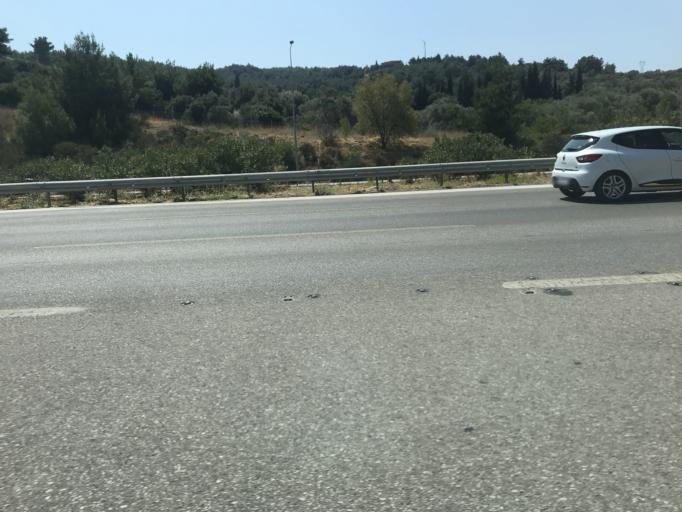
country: TR
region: Izmir
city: Urla
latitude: 38.3190
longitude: 26.7879
